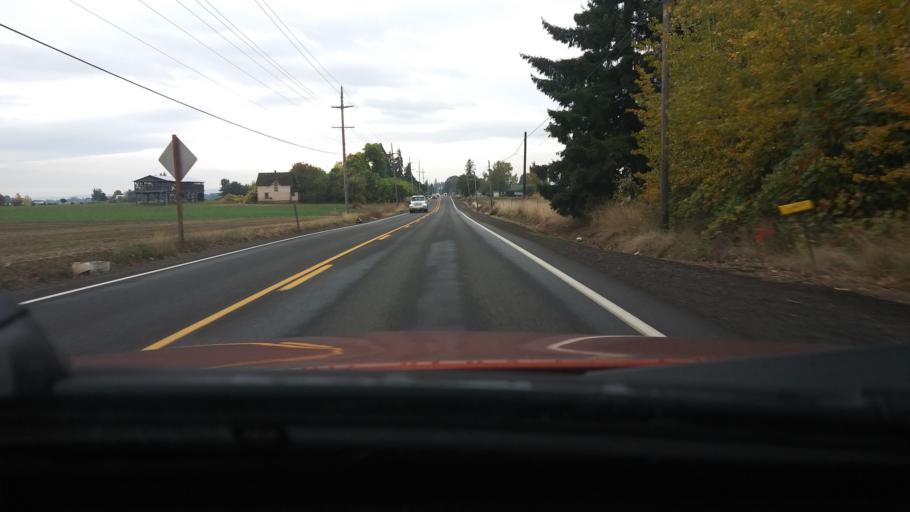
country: US
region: Oregon
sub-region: Washington County
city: Banks
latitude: 45.6010
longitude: -123.1144
